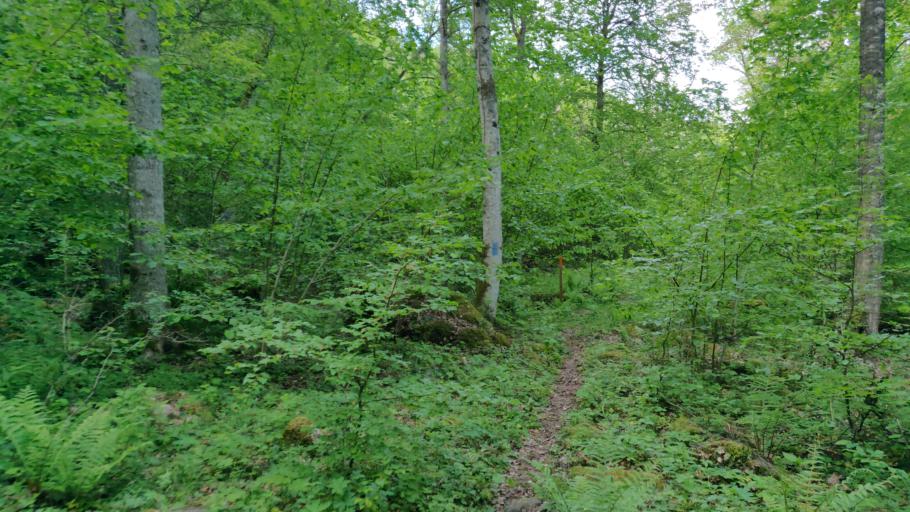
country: SE
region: Vaestra Goetaland
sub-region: Ulricehamns Kommun
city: Ulricehamn
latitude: 57.7822
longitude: 13.3806
